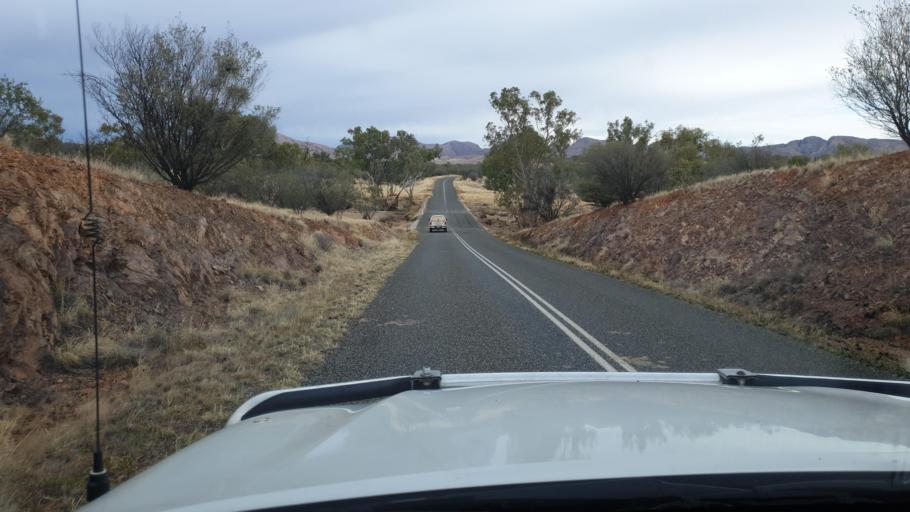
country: AU
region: Northern Territory
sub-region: Alice Springs
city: Alice Springs
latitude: -23.7827
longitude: 133.5097
